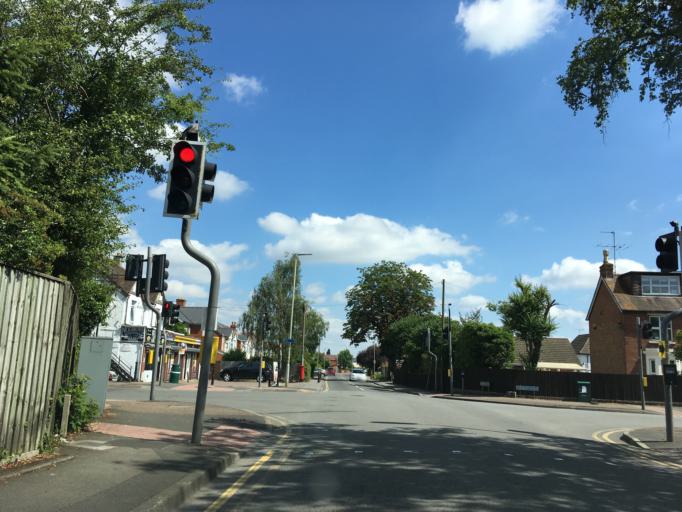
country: GB
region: England
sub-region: Gloucestershire
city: Barnwood
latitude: 51.8777
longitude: -2.2173
